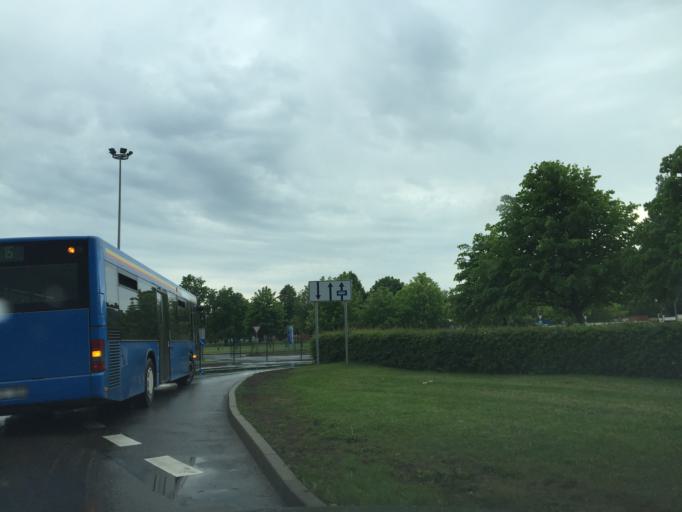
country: LT
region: Klaipedos apskritis
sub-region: Klaipeda
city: Klaipeda
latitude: 55.7550
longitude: 21.1300
